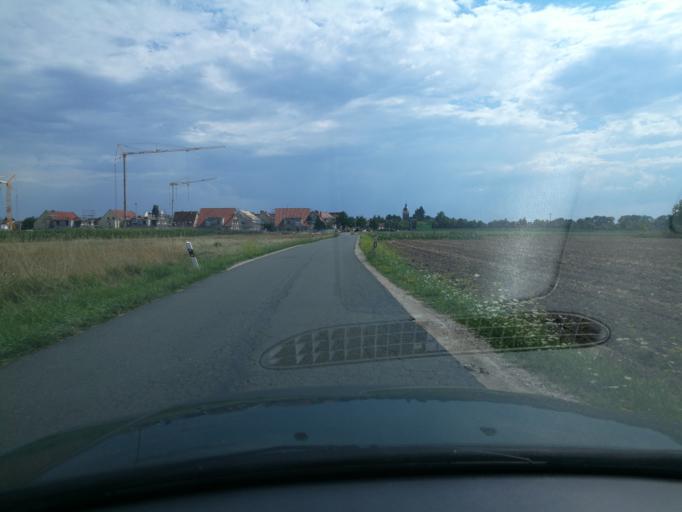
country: DE
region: Bavaria
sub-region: Regierungsbezirk Mittelfranken
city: Erlangen
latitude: 49.5367
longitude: 11.0130
